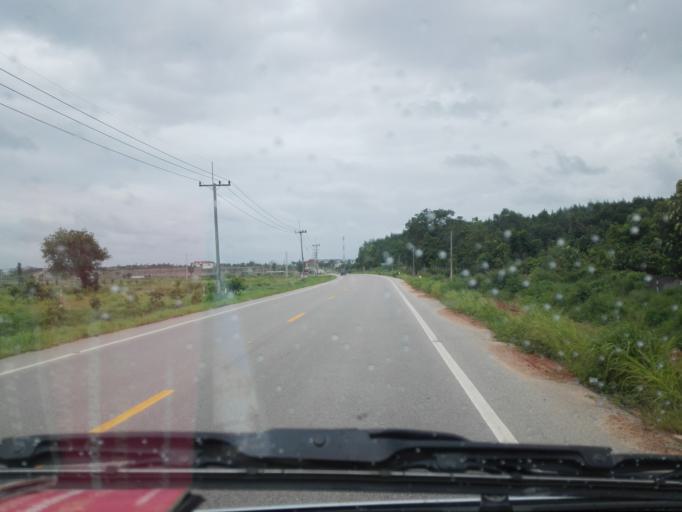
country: TH
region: Tak
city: Mae Sot
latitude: 16.6960
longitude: 98.4138
